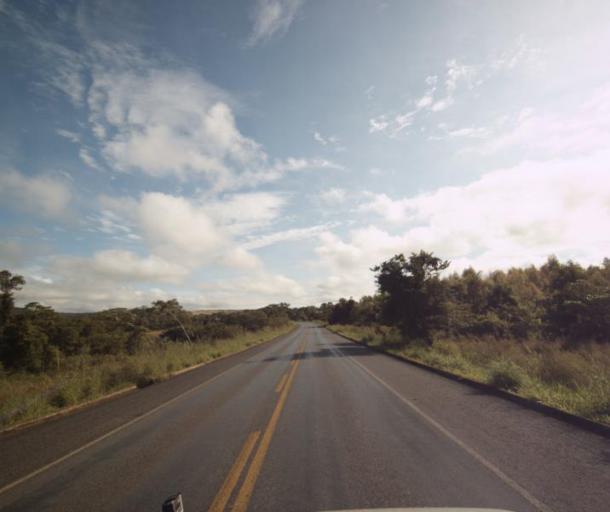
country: BR
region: Goias
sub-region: Padre Bernardo
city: Padre Bernardo
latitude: -15.4934
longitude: -48.6189
